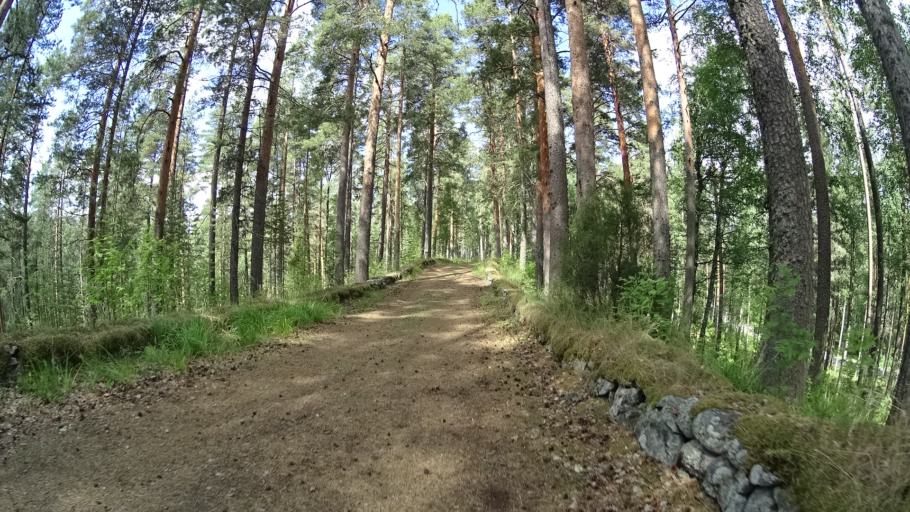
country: FI
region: Southern Savonia
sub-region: Savonlinna
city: Punkaharju
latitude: 61.7985
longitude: 29.3095
